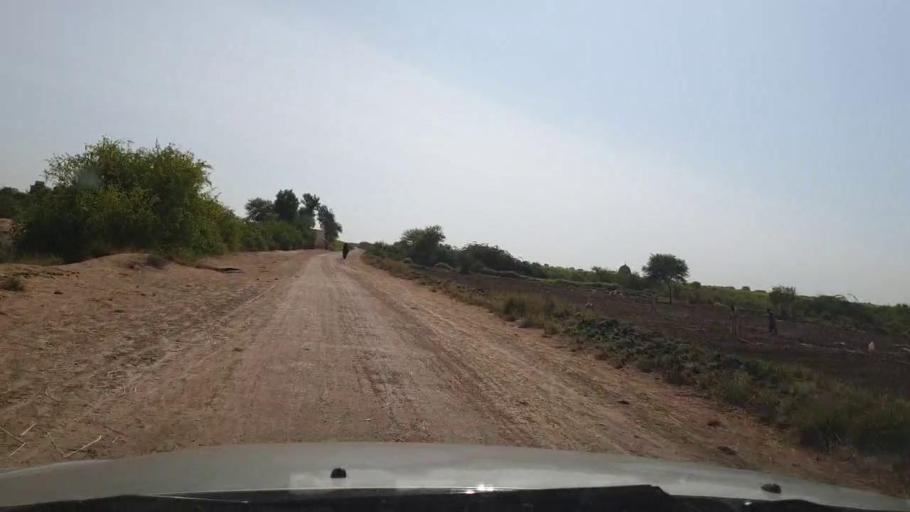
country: PK
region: Sindh
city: Bulri
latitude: 25.0025
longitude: 68.3197
